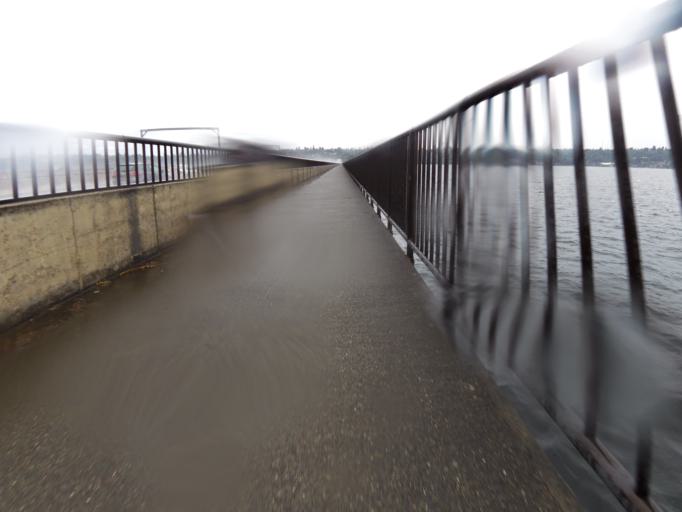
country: US
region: Washington
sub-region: King County
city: Mercer Island
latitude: 47.5902
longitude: -122.2650
